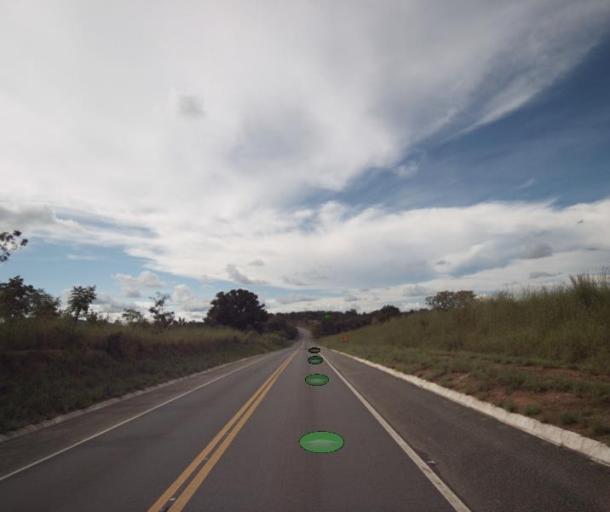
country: BR
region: Goias
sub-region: Barro Alto
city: Barro Alto
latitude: -15.1698
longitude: -48.7025
